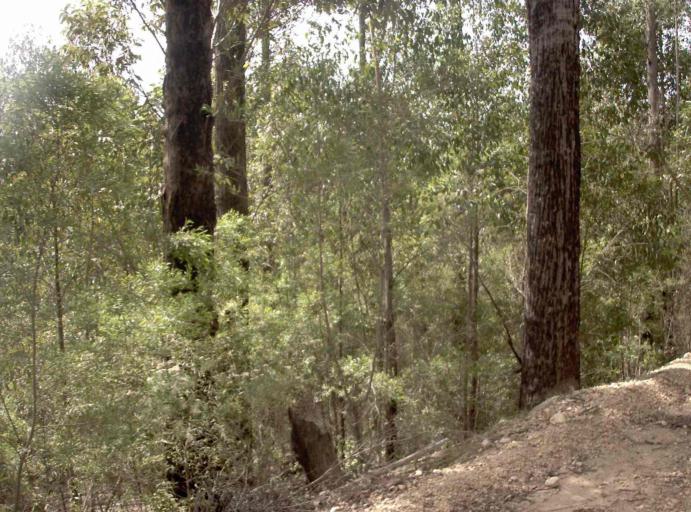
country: AU
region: Victoria
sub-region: East Gippsland
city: Lakes Entrance
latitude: -37.6152
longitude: 148.6988
